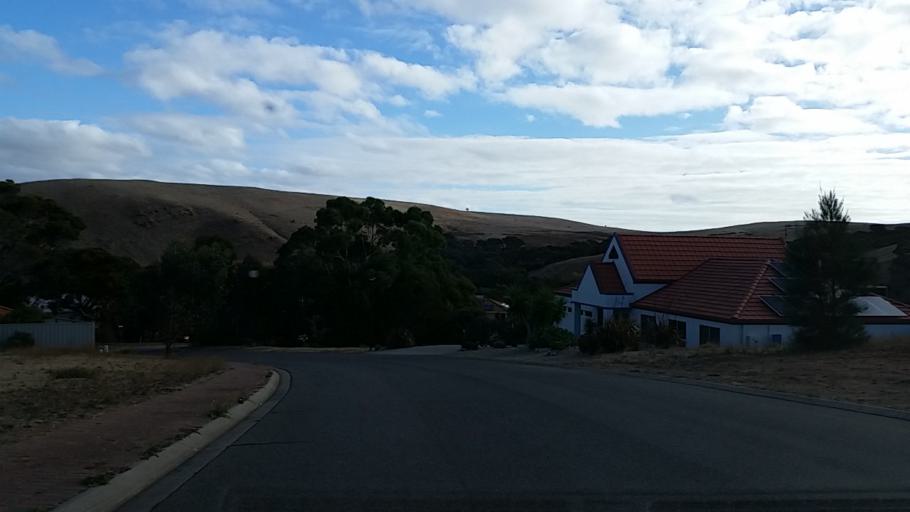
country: AU
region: South Australia
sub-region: Yankalilla
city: Normanville
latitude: -35.5048
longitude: 138.2462
